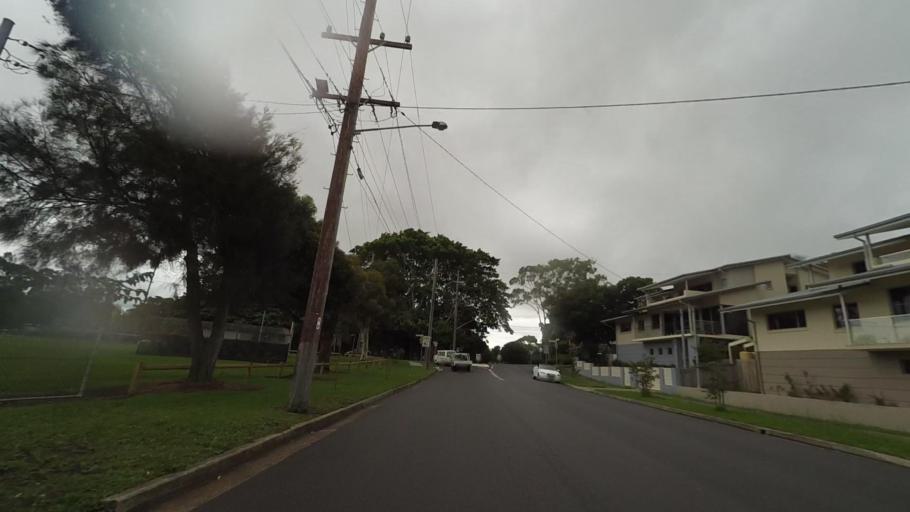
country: AU
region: New South Wales
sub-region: Kogarah
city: Beverly Park
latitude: -33.9843
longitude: 151.1327
